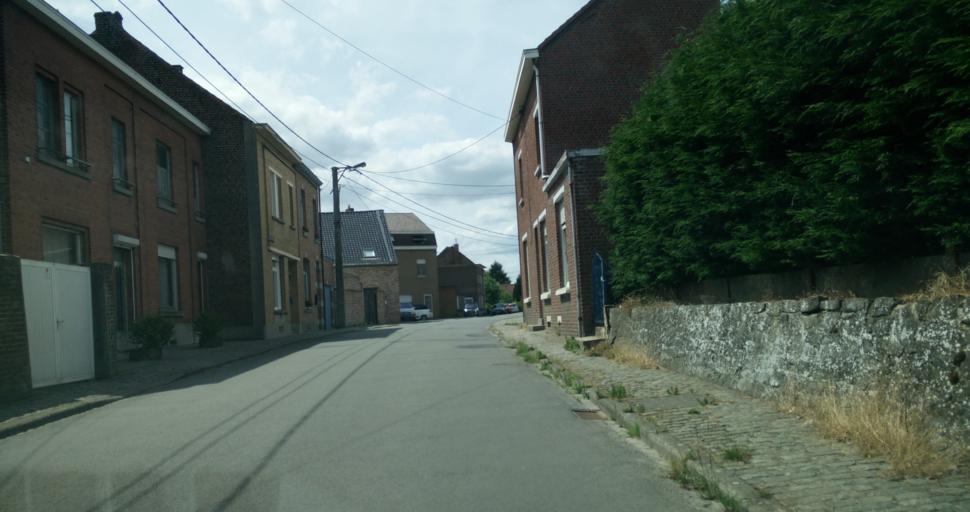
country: BE
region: Wallonia
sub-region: Province du Hainaut
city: Lessines
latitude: 50.7304
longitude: 3.8477
